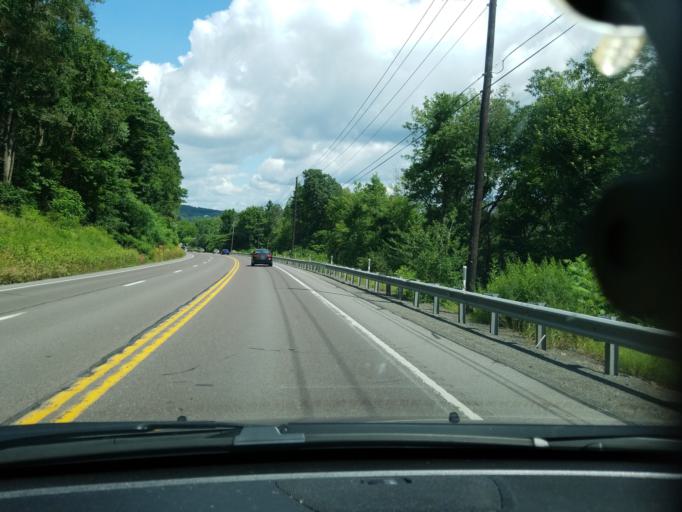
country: US
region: Pennsylvania
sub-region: Northumberland County
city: Kulpmont
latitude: 40.8278
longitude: -76.5030
